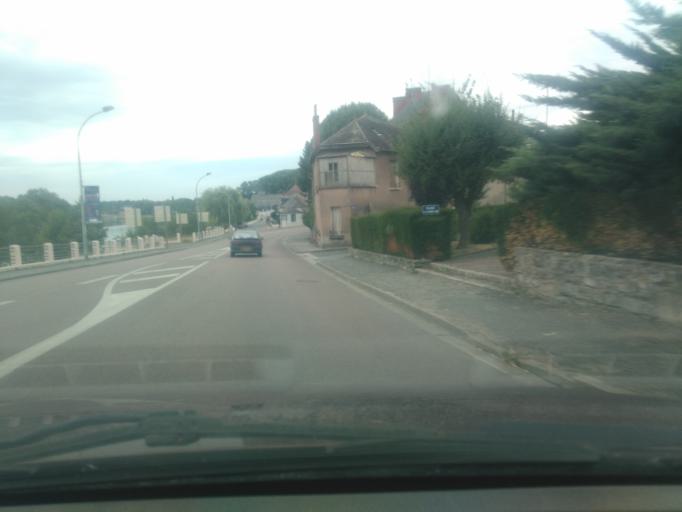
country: FR
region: Bourgogne
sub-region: Departement de la Nievre
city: Decize
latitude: 46.8283
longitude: 3.4588
